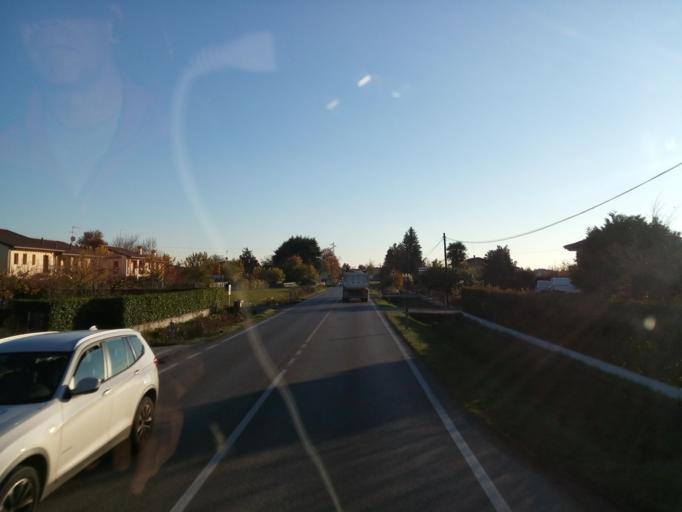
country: IT
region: Veneto
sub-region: Provincia di Treviso
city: Caerano di San Marco
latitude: 45.7924
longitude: 11.9942
